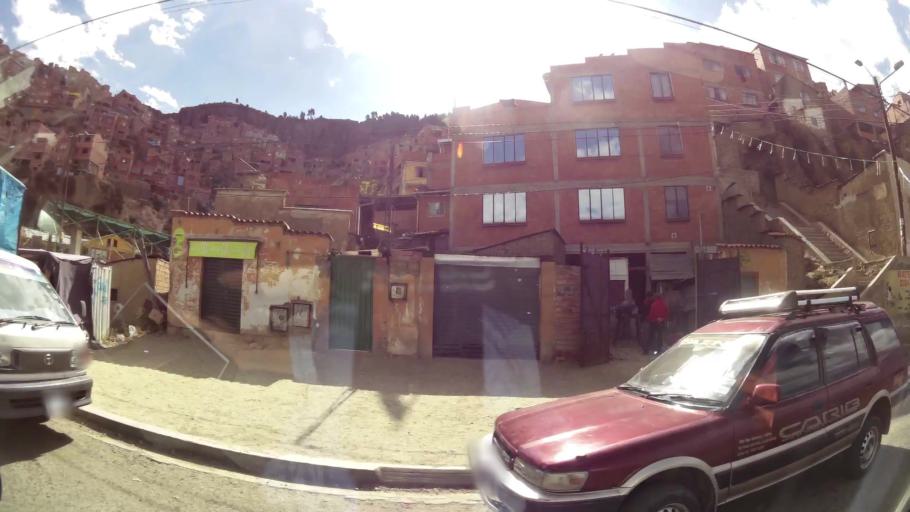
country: BO
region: La Paz
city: La Paz
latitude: -16.4825
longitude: -68.1294
